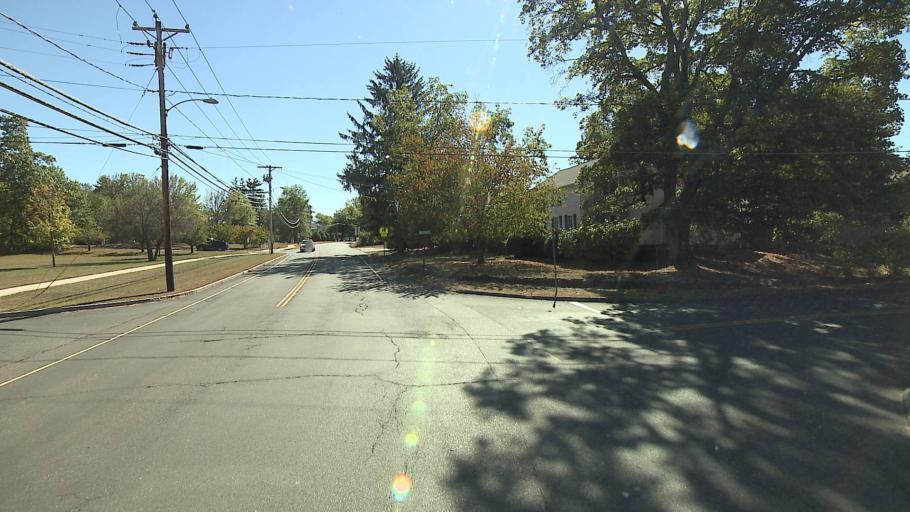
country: US
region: Connecticut
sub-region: Hartford County
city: Weatogue
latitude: 41.8116
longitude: -72.8305
